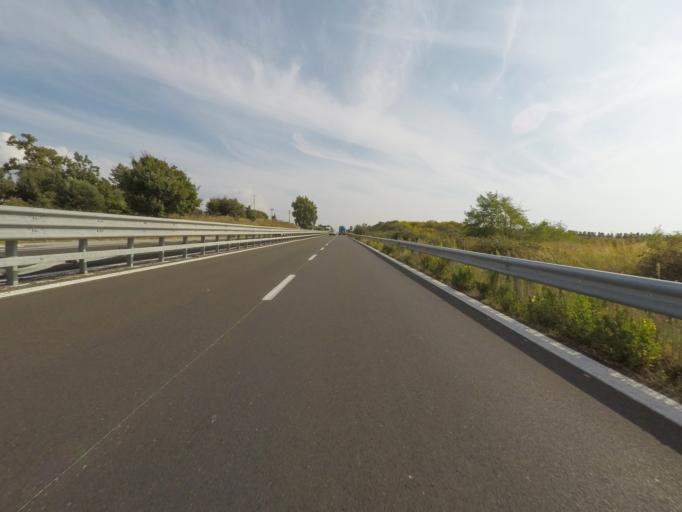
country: IT
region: Latium
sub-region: Provincia di Viterbo
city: Montalto di Castro
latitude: 42.3334
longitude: 11.6258
